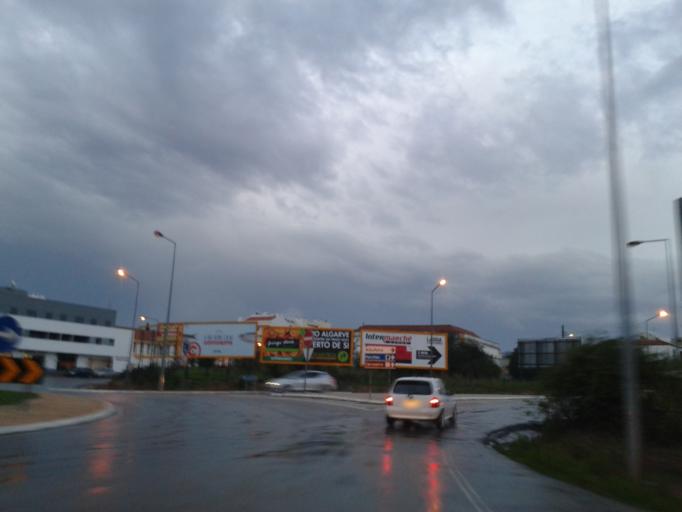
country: PT
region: Faro
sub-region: Lagoa
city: Lagoa
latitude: 37.1346
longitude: -8.4593
